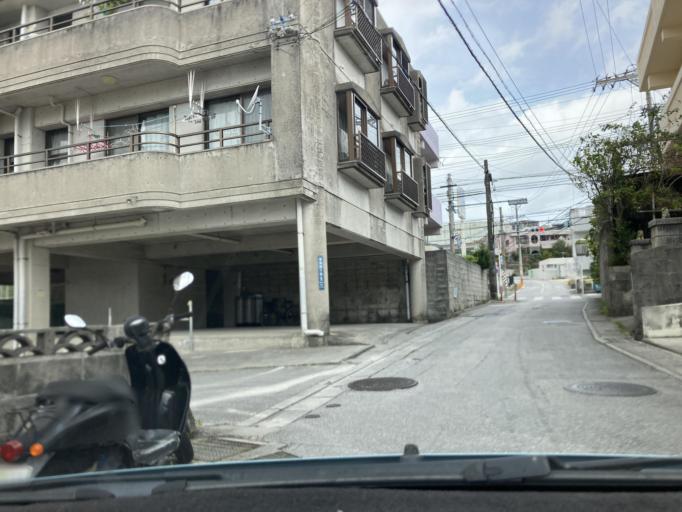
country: JP
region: Okinawa
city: Ginowan
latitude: 26.2373
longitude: 127.7371
